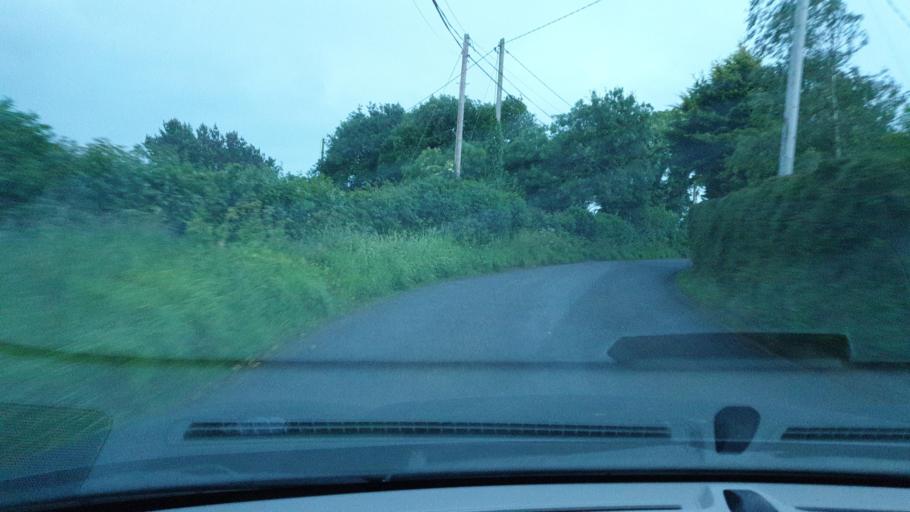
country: IE
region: Leinster
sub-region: An Mhi
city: Ashbourne
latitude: 53.5352
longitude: -6.3360
